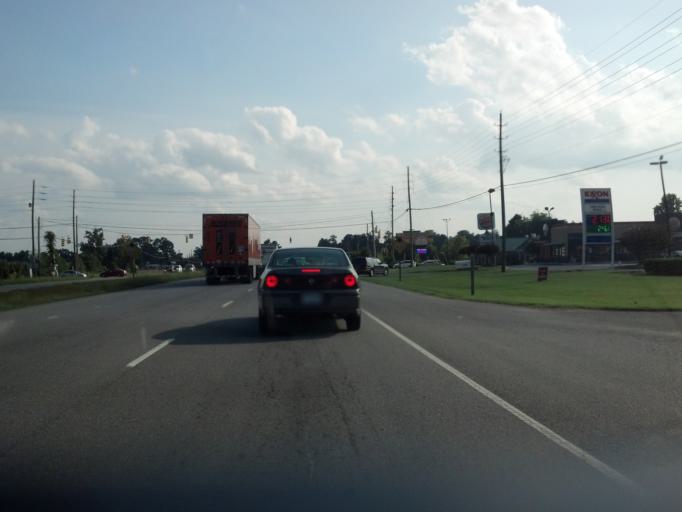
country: US
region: North Carolina
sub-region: Pitt County
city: Greenville
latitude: 35.6540
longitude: -77.3652
